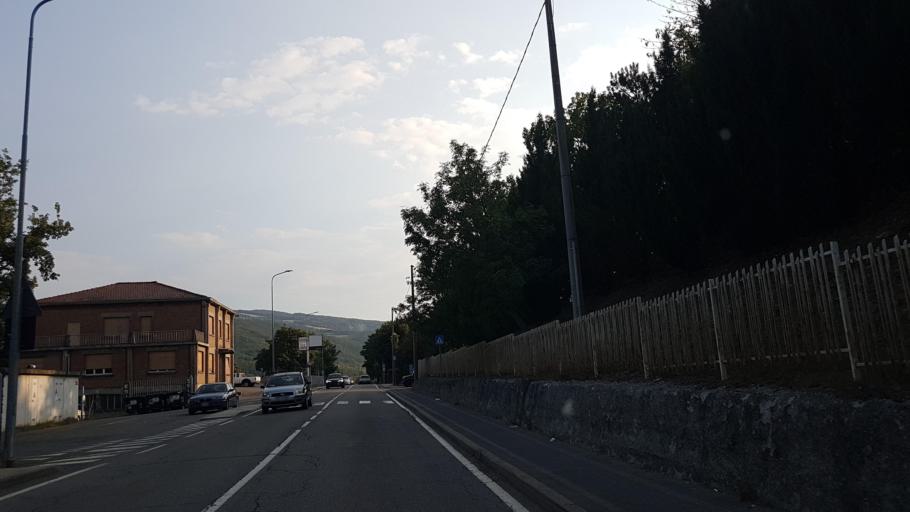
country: IT
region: Emilia-Romagna
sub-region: Provincia di Parma
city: Solignano
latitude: 44.6122
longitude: 9.9772
